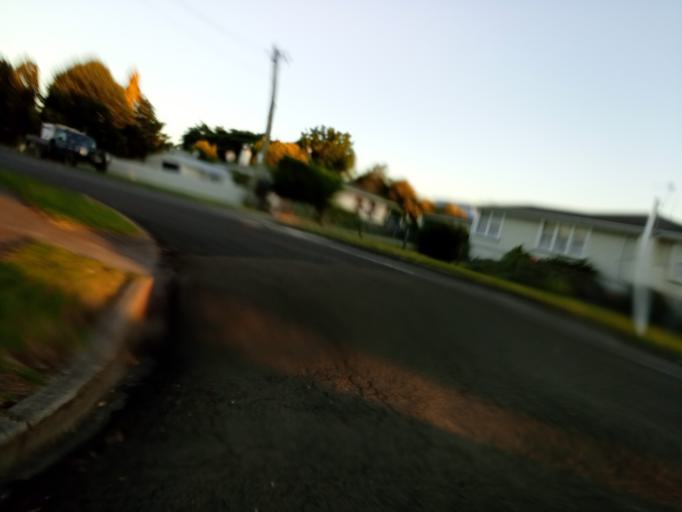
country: NZ
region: Gisborne
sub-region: Gisborne District
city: Gisborne
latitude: -38.6418
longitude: 178.0026
